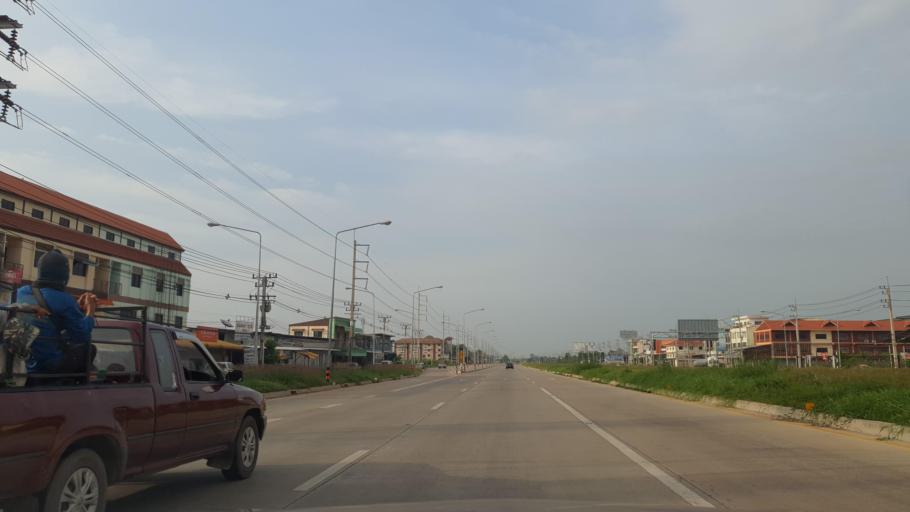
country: TH
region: Phitsanulok
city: Phitsanulok
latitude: 16.8171
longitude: 100.3311
